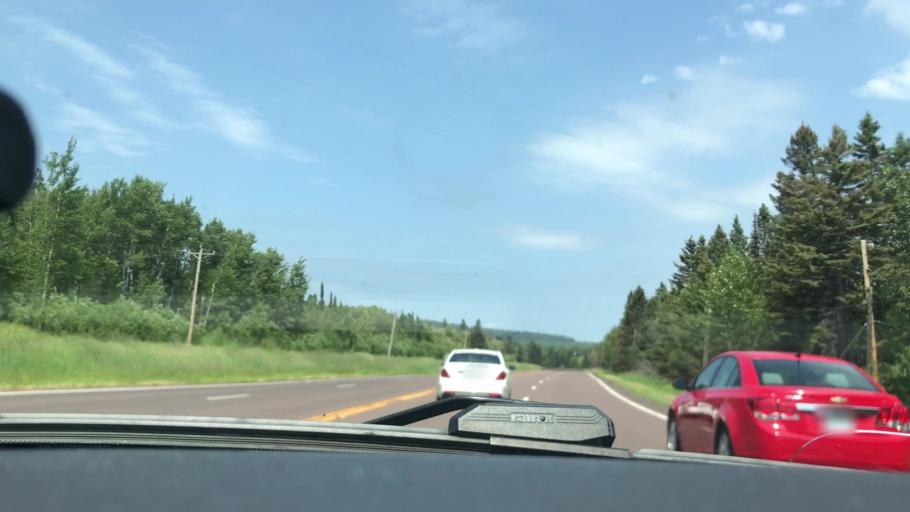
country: US
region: Minnesota
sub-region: Lake County
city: Two Harbors
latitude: 47.0807
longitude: -91.5846
